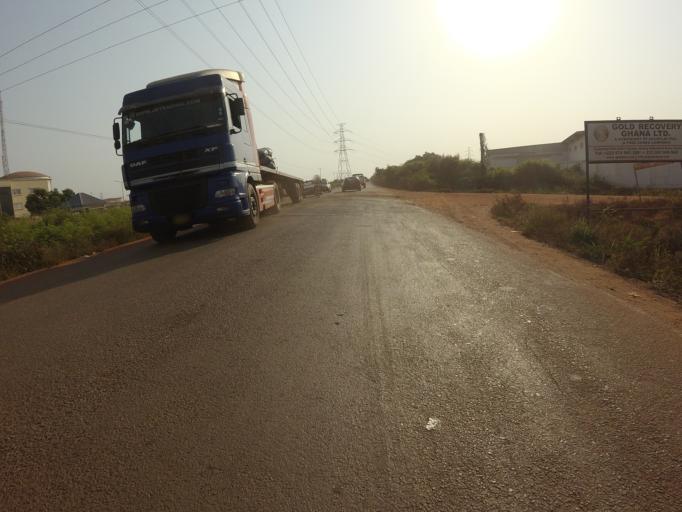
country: GH
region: Greater Accra
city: Tema
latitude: 5.6803
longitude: 0.0391
